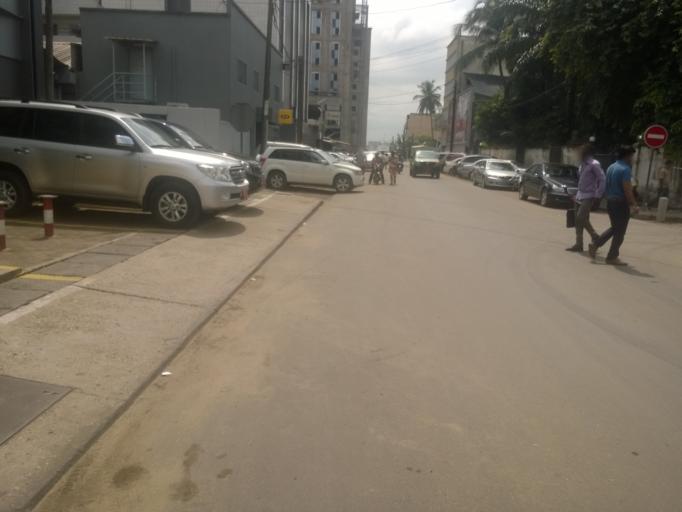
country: CM
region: Littoral
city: Douala
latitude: 4.0559
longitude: 9.7001
